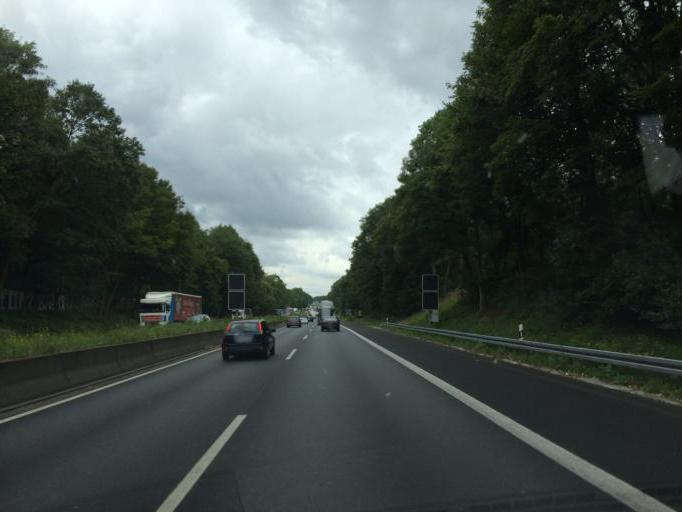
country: DE
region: North Rhine-Westphalia
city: Castrop-Rauxel
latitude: 51.4967
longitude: 7.3025
